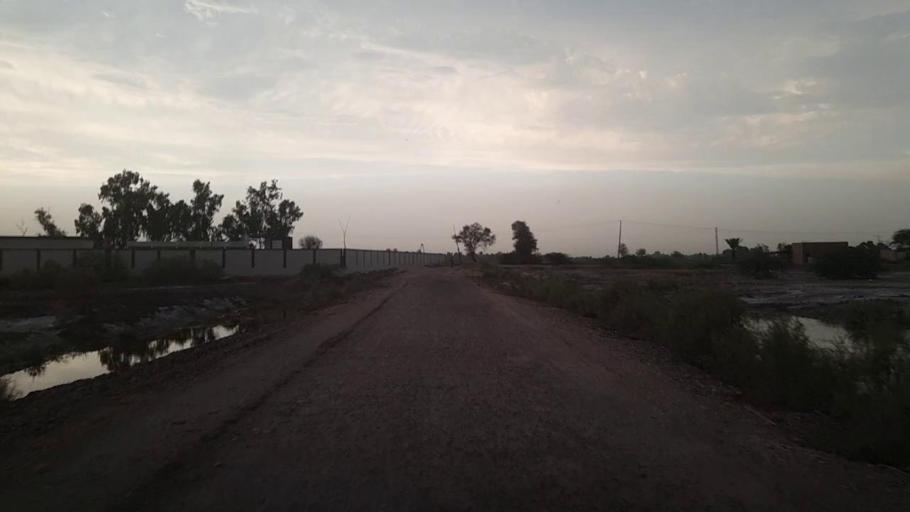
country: PK
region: Sindh
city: Karaundi
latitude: 27.0440
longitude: 68.3803
